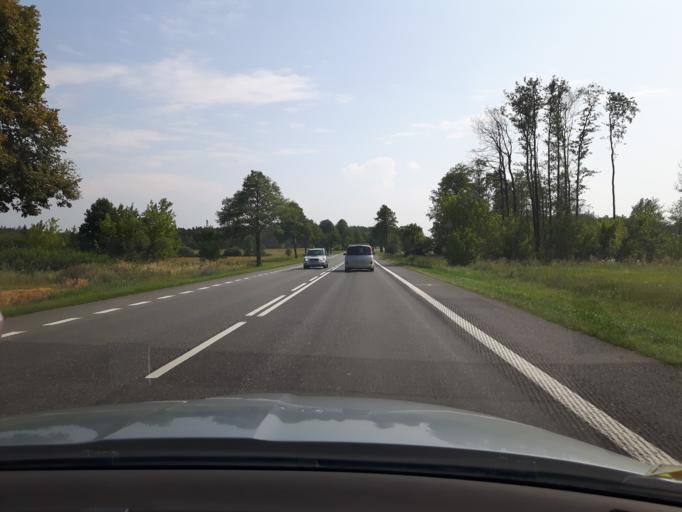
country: PL
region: Masovian Voivodeship
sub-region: Powiat mlawski
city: Strzegowo
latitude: 52.9317
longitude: 20.2852
